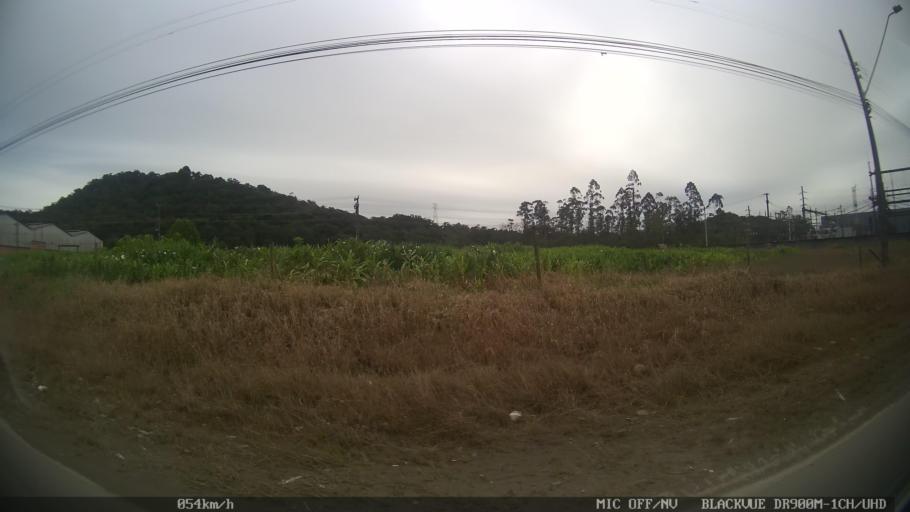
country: BR
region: Santa Catarina
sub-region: Joinville
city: Joinville
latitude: -26.2312
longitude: -48.9102
